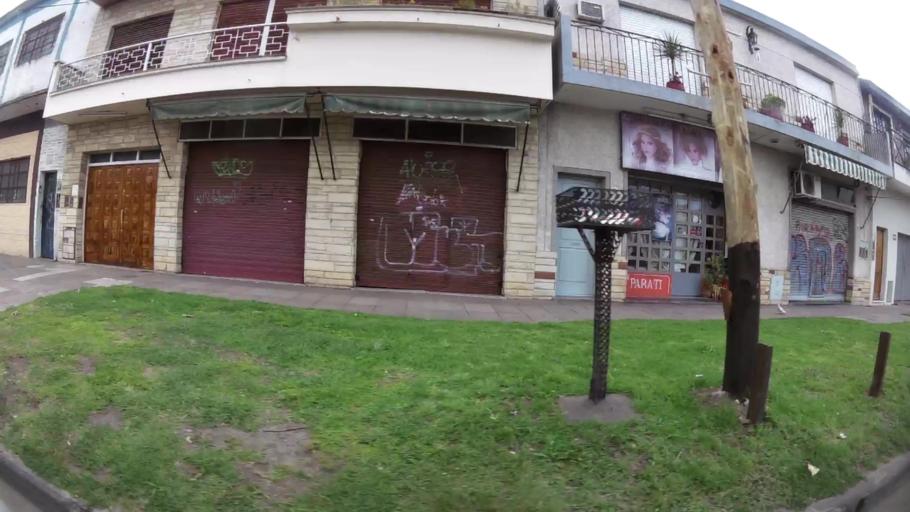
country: AR
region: Buenos Aires
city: Ituzaingo
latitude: -34.6429
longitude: -58.6721
